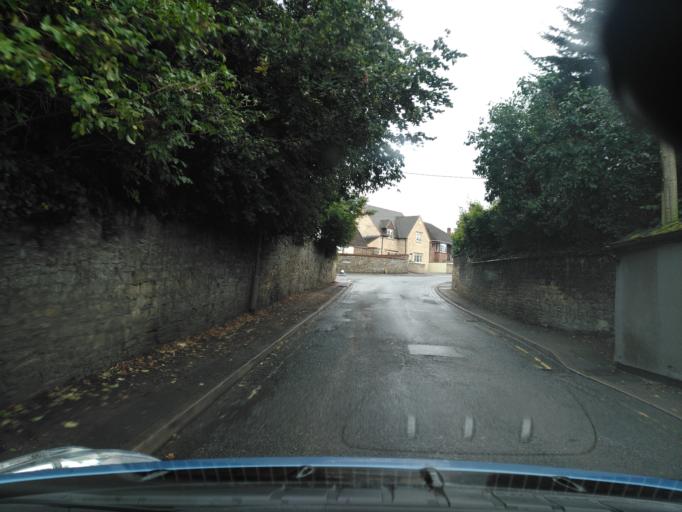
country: GB
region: England
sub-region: Oxfordshire
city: Wheatley
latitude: 51.7471
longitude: -1.1392
